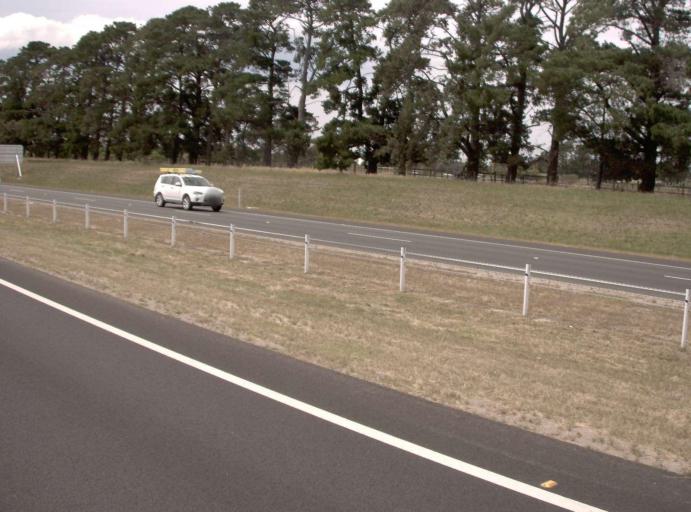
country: AU
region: Victoria
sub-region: Mornington Peninsula
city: Moorooduc
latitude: -38.2190
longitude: 145.1285
